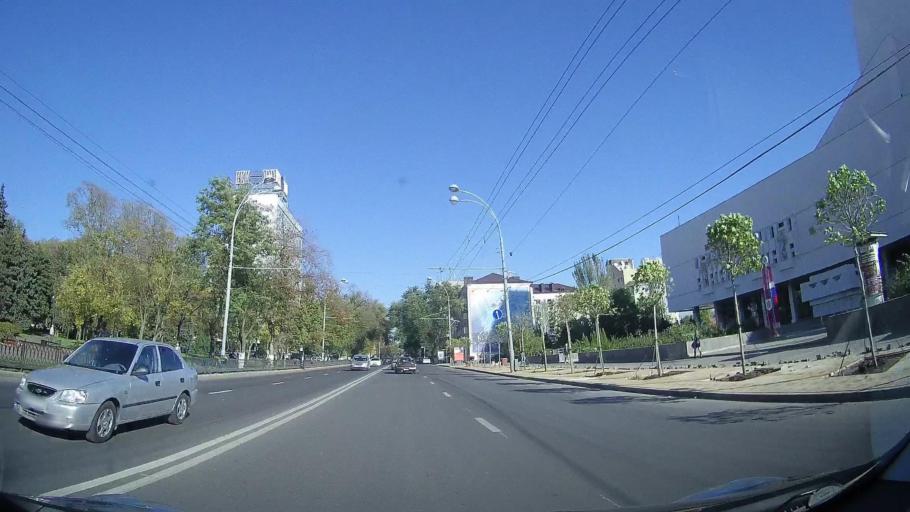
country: RU
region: Rostov
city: Rostov-na-Donu
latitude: 47.2253
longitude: 39.7323
